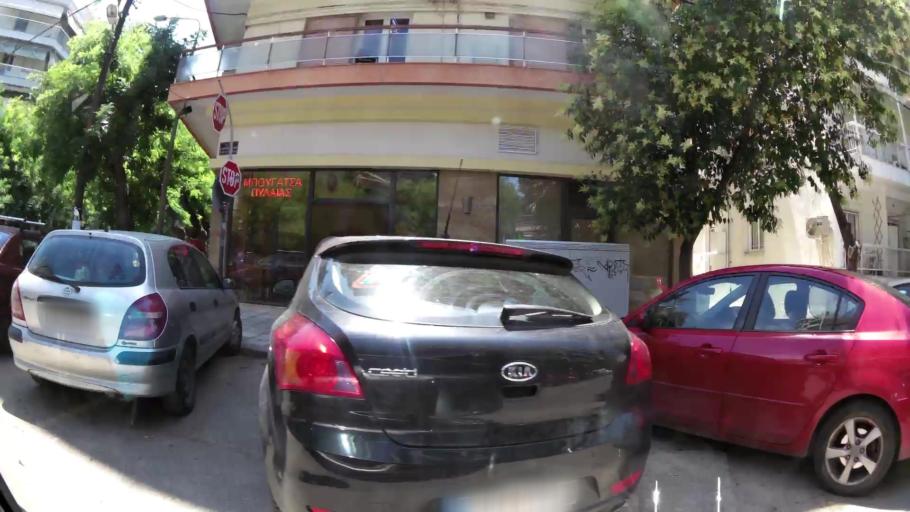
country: GR
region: Central Macedonia
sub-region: Nomos Thessalonikis
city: Triandria
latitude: 40.6089
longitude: 22.9588
